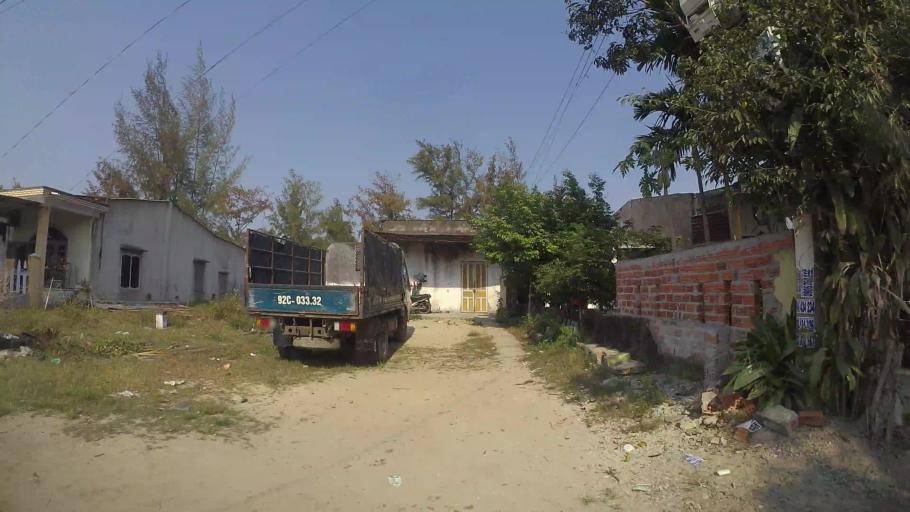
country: VN
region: Quang Nam
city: Quang Nam
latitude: 15.9507
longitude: 108.2671
